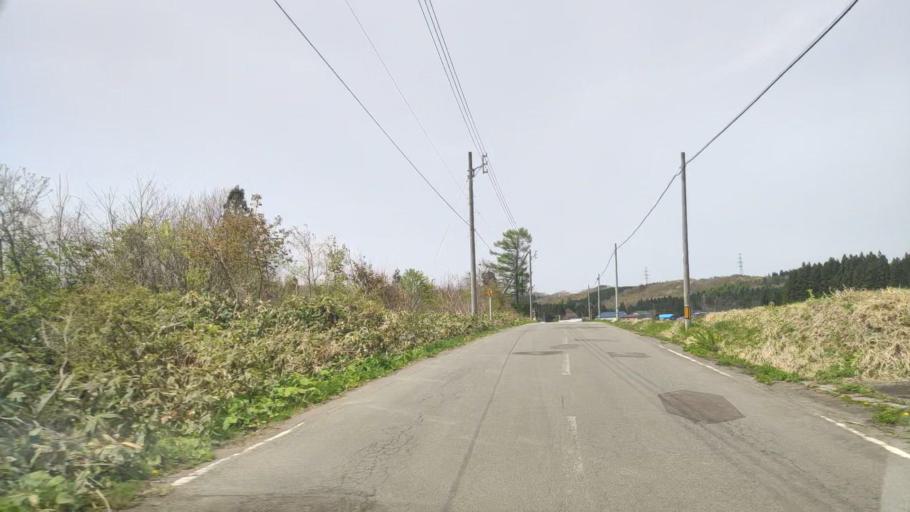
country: JP
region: Aomori
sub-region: Misawa Shi
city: Inuotose
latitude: 40.7849
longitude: 141.1133
